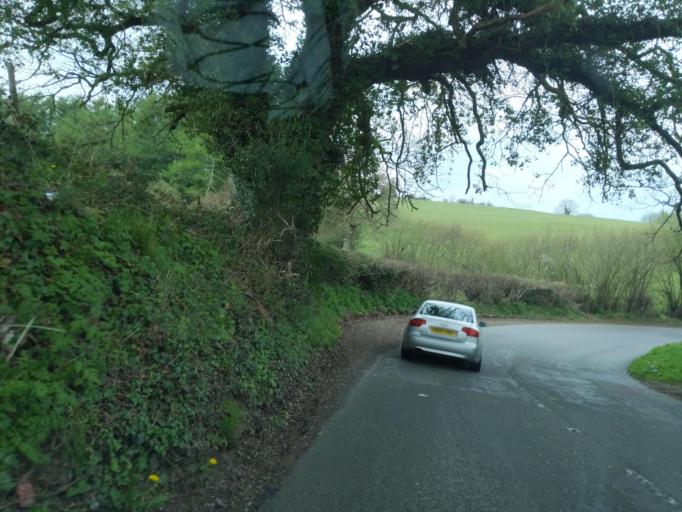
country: GB
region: England
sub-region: Devon
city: Bovey Tracey
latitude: 50.6568
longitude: -3.7806
